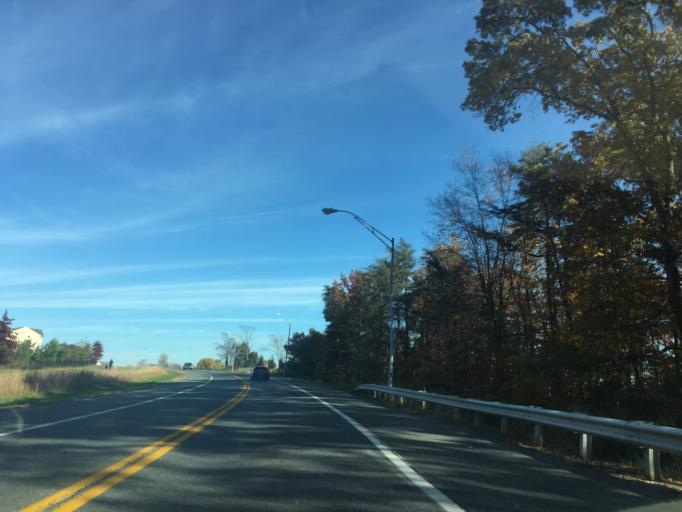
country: US
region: Maryland
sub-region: Baltimore County
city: Overlea
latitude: 39.3624
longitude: -76.4949
